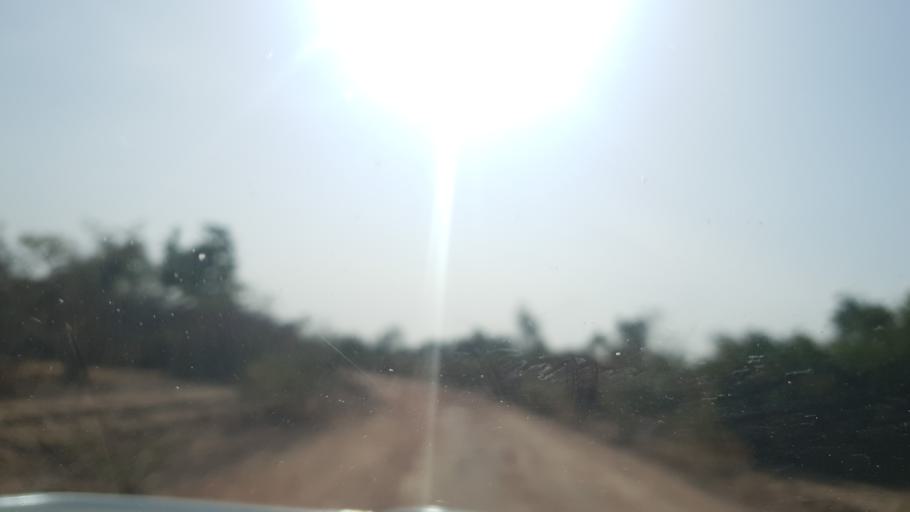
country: ML
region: Koulikoro
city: Dioila
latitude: 12.7110
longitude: -6.7871
